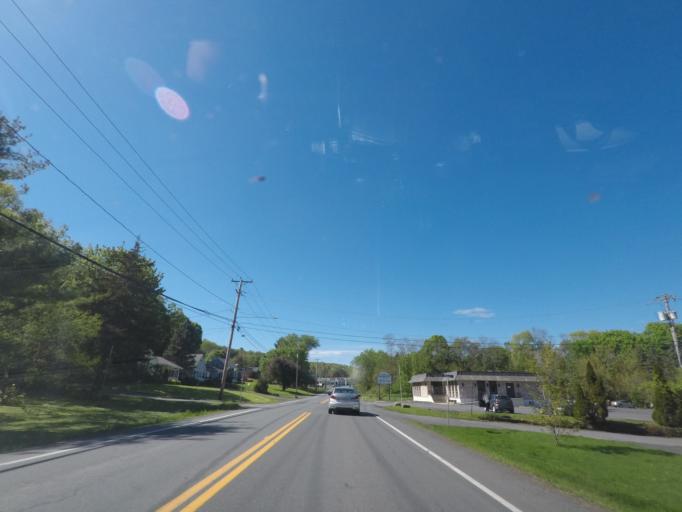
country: US
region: New York
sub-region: Albany County
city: Ravena
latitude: 42.4715
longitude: -73.8174
